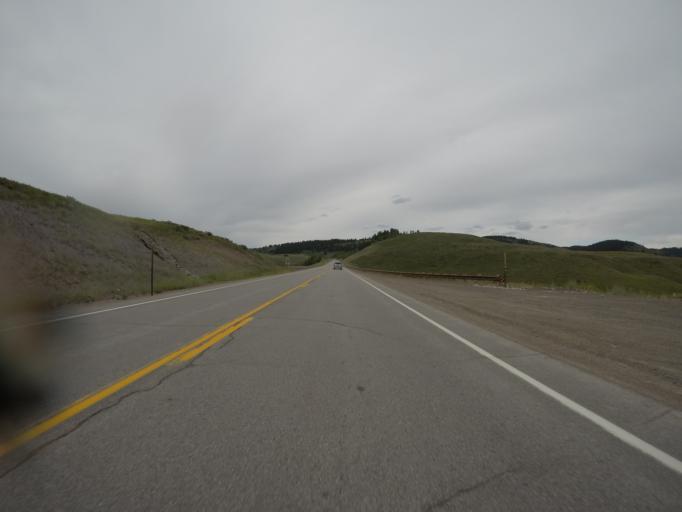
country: US
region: Wyoming
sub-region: Lincoln County
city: Afton
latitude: 42.4869
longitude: -110.9222
